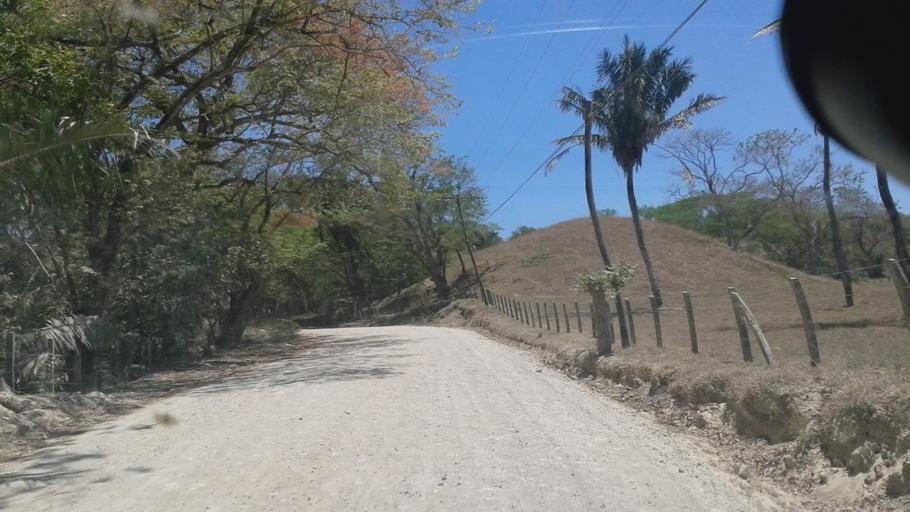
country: CR
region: Guanacaste
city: Samara
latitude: 9.9954
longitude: -85.6846
